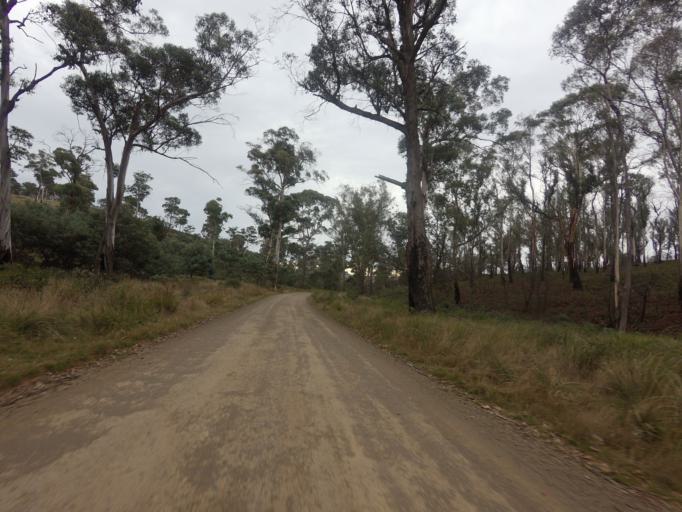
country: AU
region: Tasmania
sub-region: Derwent Valley
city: New Norfolk
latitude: -42.5606
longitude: 146.9599
